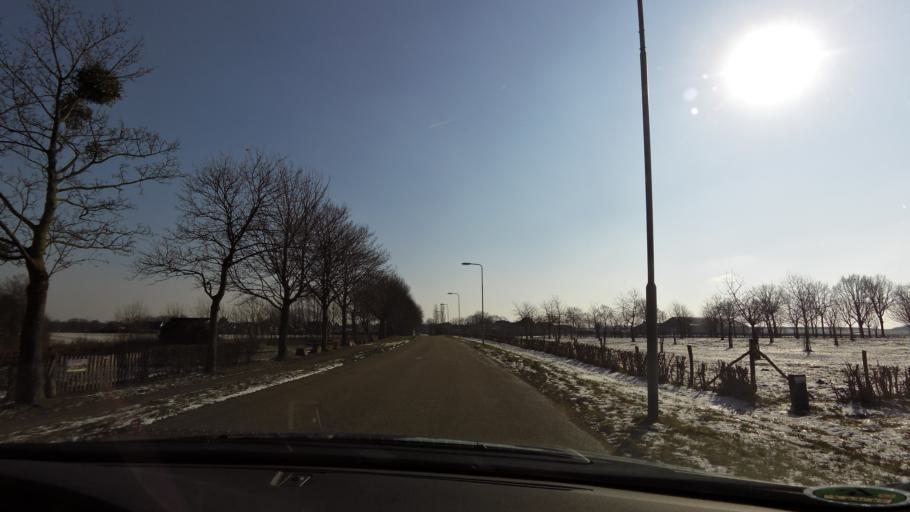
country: NL
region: Limburg
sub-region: Valkenburg aan de Geul
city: Houthem
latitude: 50.8598
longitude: 5.7994
